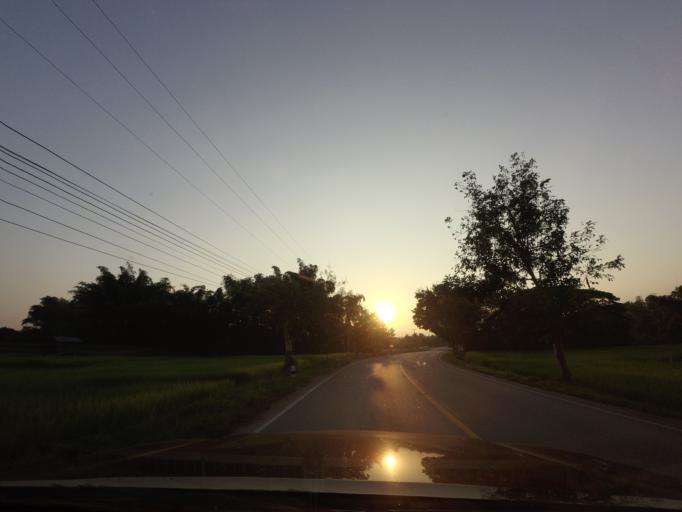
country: TH
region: Nan
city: Na Noi
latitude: 18.3259
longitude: 100.7252
